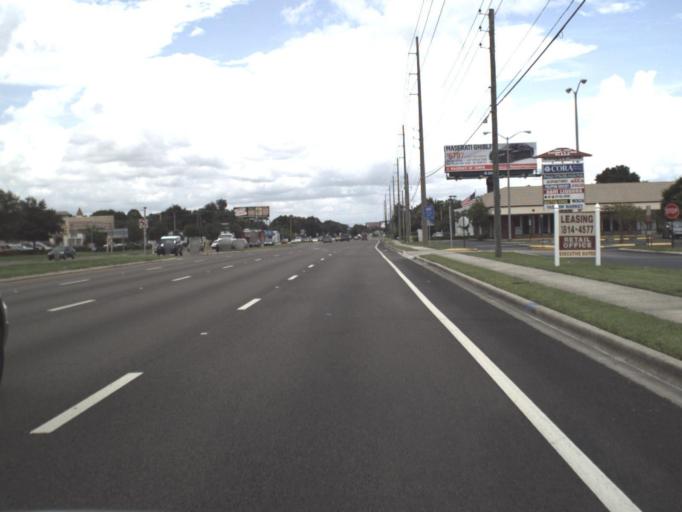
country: US
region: Florida
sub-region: Pinellas County
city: Oldsmar
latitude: 28.0331
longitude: -82.6474
